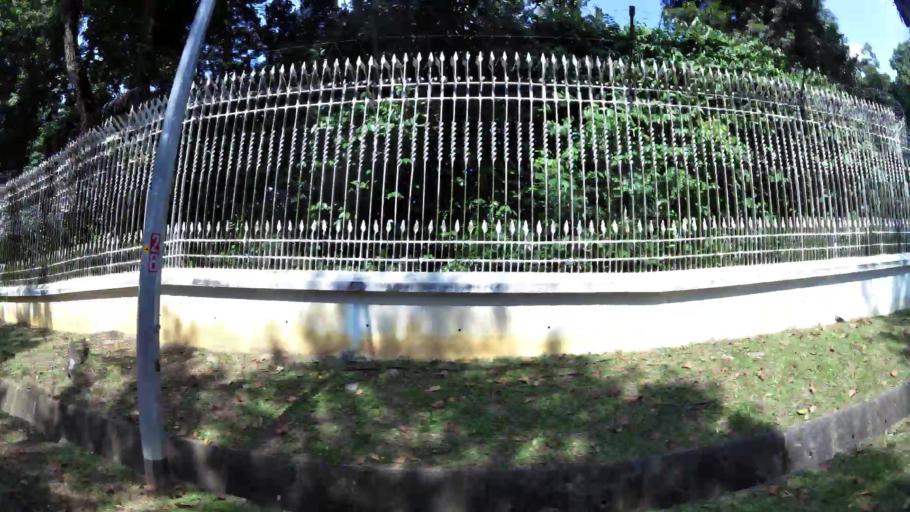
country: SG
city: Singapore
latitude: 1.3046
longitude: 103.8457
